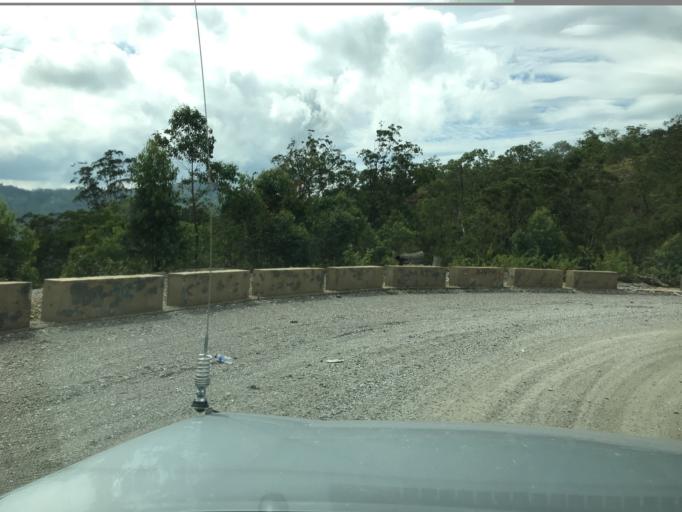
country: TL
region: Aileu
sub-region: Aileu Villa
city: Aileu
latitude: -8.6643
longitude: 125.5423
